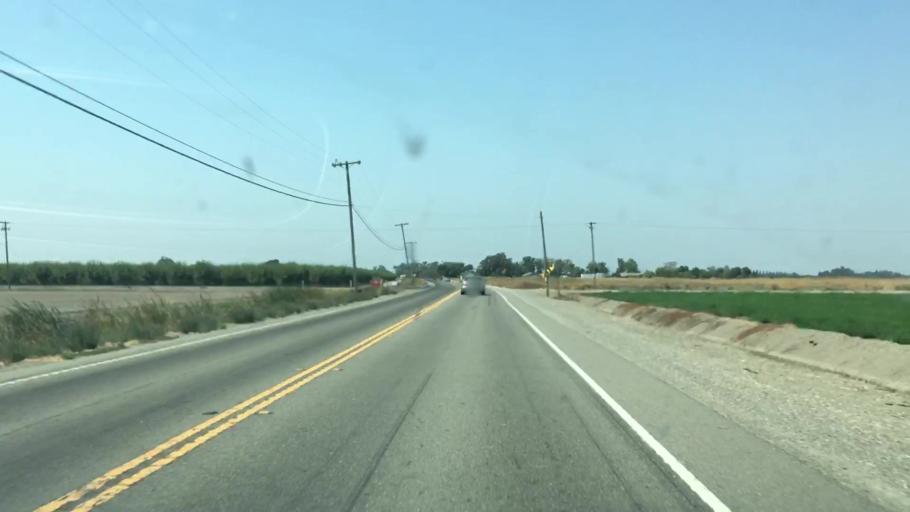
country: US
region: California
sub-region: San Joaquin County
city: Taft Mosswood
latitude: 37.8774
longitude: -121.3657
